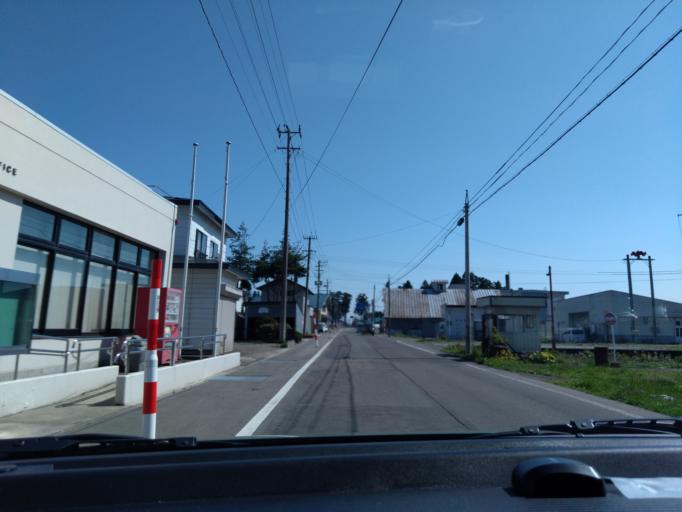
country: JP
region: Akita
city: Kakunodatemachi
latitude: 39.5549
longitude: 140.5860
